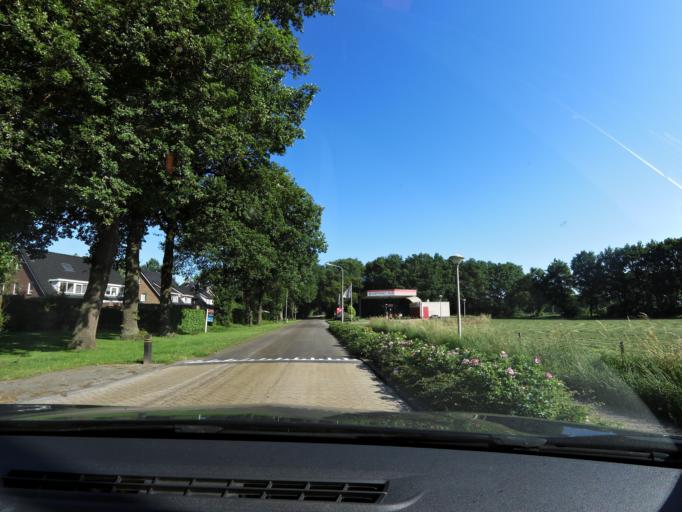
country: NL
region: Overijssel
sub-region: Gemeente Raalte
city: Raalte
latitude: 52.3227
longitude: 6.3492
